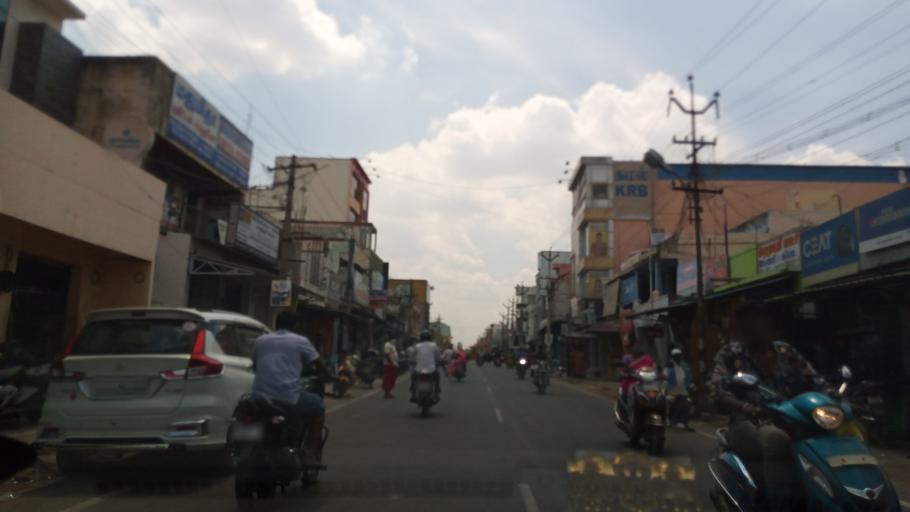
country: IN
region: Tamil Nadu
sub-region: Vellore
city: Walajapet
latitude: 12.9252
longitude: 79.3670
